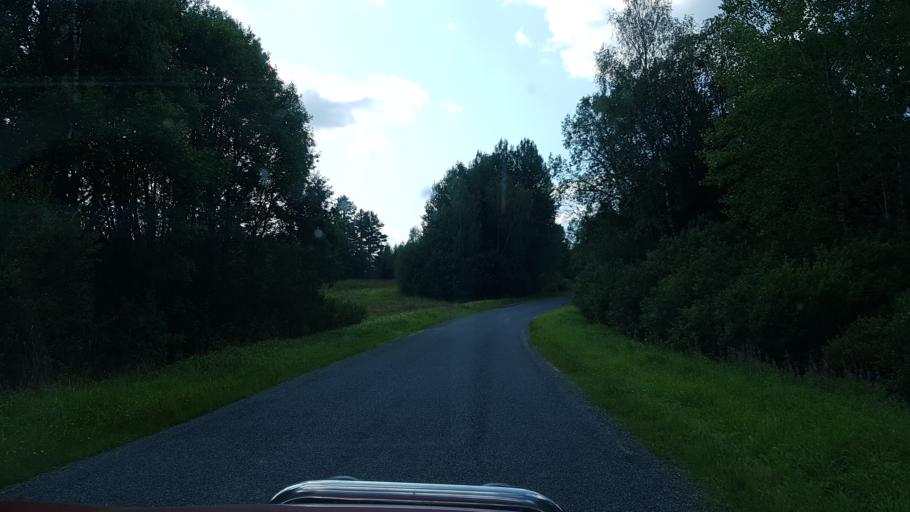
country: LV
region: Aluksnes Rajons
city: Aluksne
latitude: 57.6016
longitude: 27.0958
